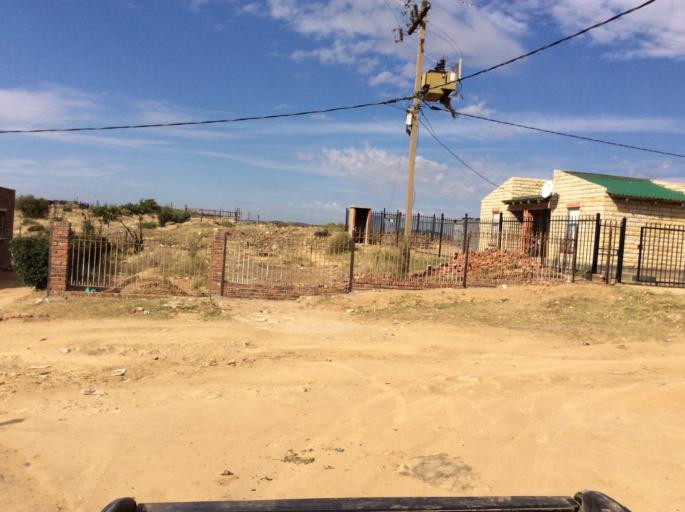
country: LS
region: Mafeteng
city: Mafeteng
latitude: -29.7189
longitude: 27.0179
